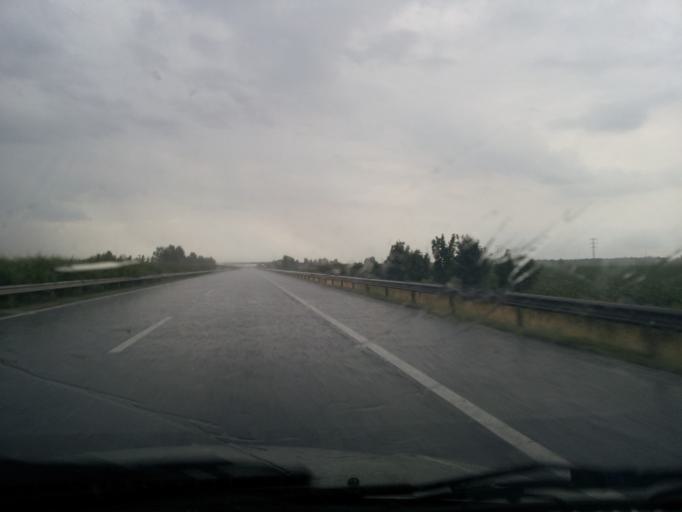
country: HU
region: Borsod-Abauj-Zemplen
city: Malyi
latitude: 48.0197
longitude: 20.8711
